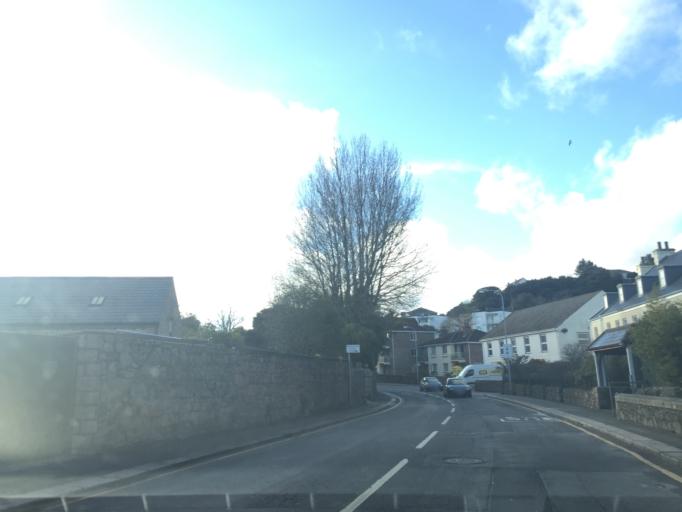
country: JE
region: St Helier
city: Saint Helier
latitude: 49.1980
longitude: -2.1353
